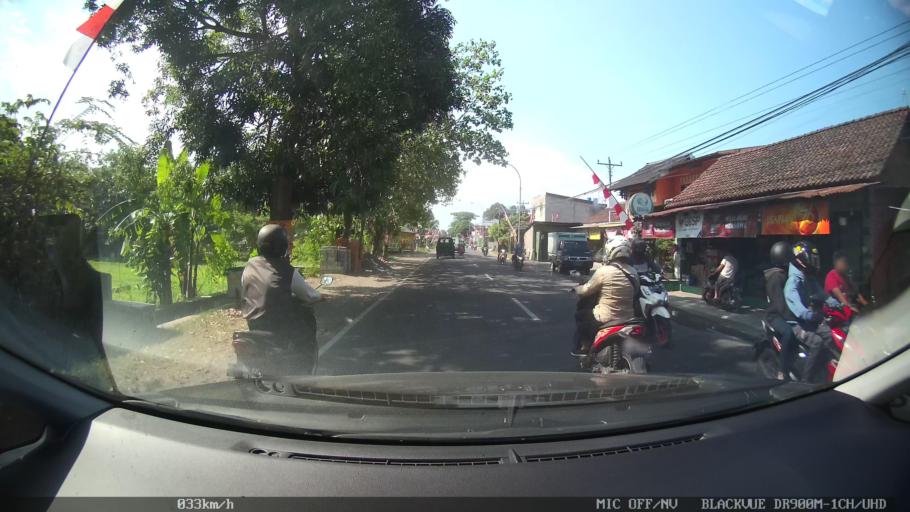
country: ID
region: Daerah Istimewa Yogyakarta
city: Sewon
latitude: -7.8806
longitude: 110.3898
